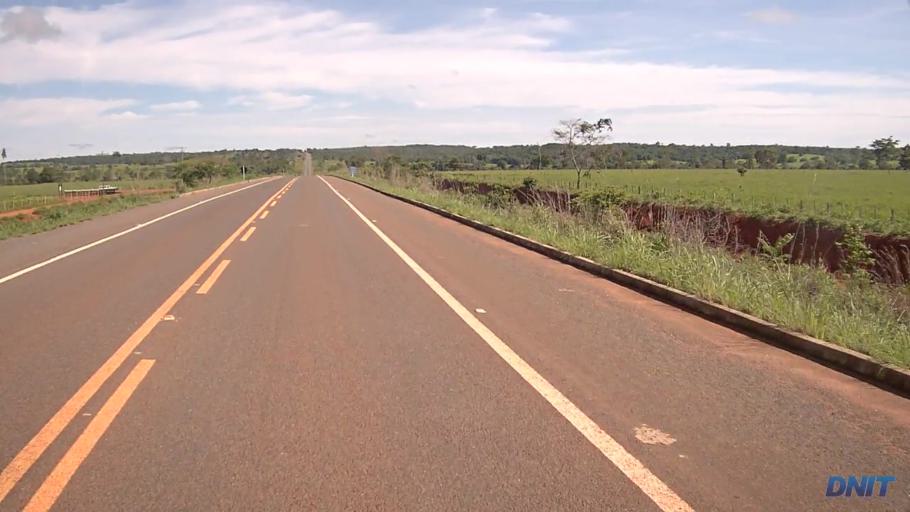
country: BR
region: Goias
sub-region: Sao Miguel Do Araguaia
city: Sao Miguel do Araguaia
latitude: -13.3562
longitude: -50.1479
